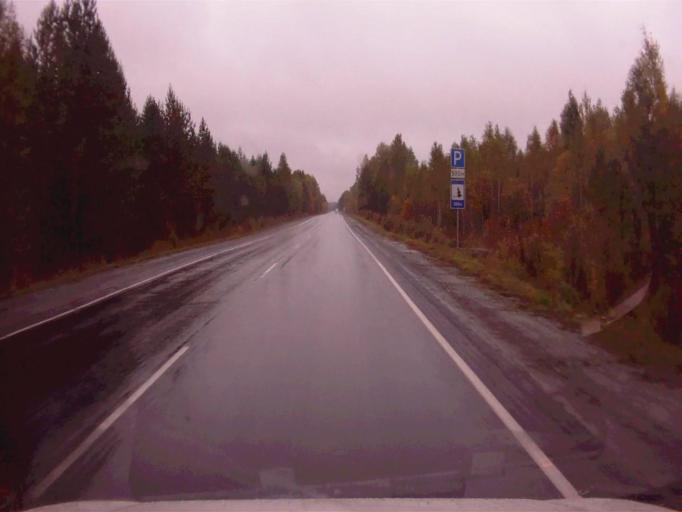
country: RU
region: Chelyabinsk
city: Tayginka
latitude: 55.5406
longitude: 60.6466
